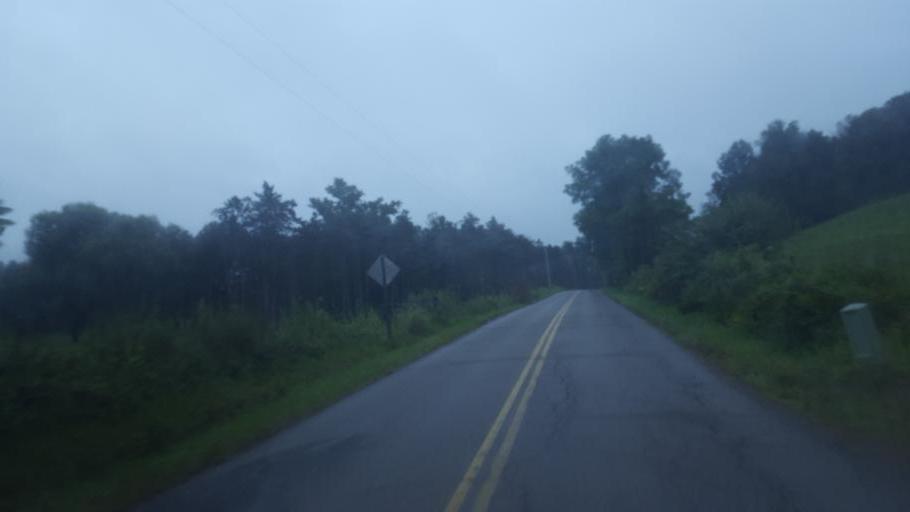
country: US
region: Ohio
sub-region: Jackson County
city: Jackson
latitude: 38.9982
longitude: -82.6173
